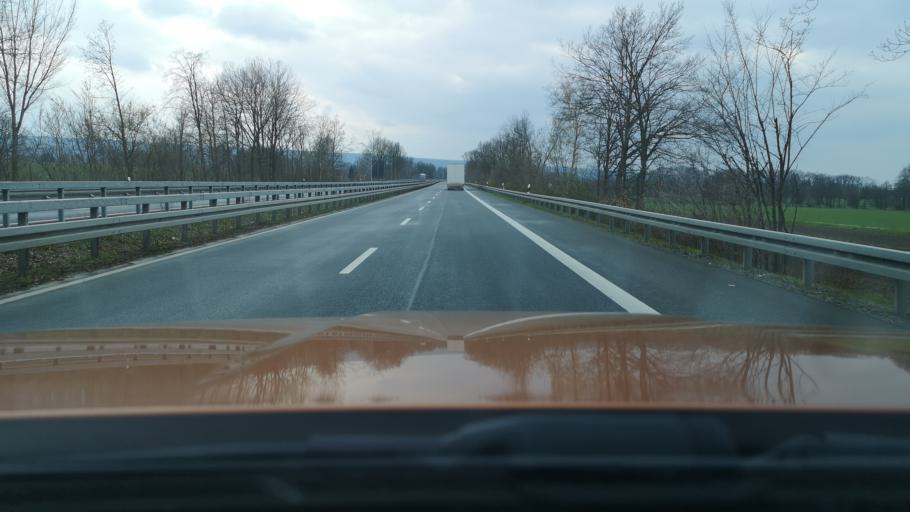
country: DE
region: Lower Saxony
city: Stadthagen
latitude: 52.3238
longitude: 9.2302
